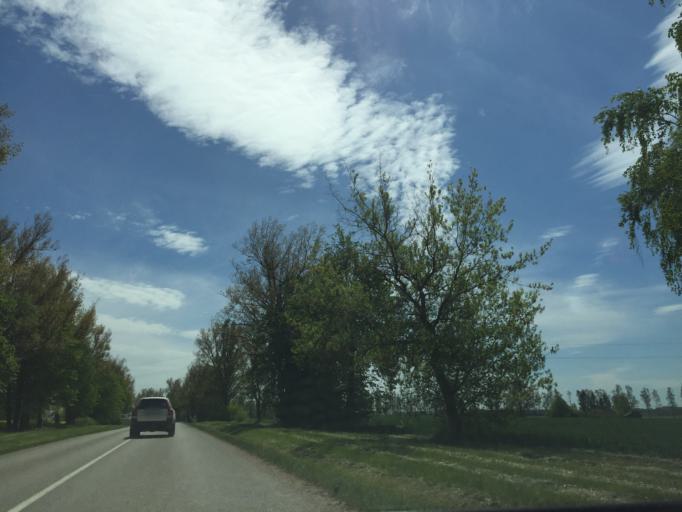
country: LT
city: Linkuva
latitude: 56.0495
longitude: 24.1152
